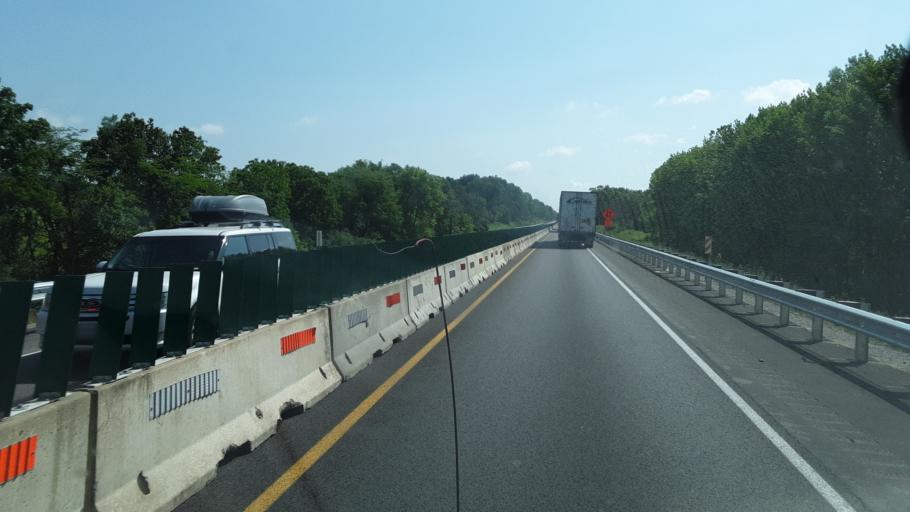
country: US
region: Illinois
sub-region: Effingham County
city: Altamont
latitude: 39.0597
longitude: -88.6962
